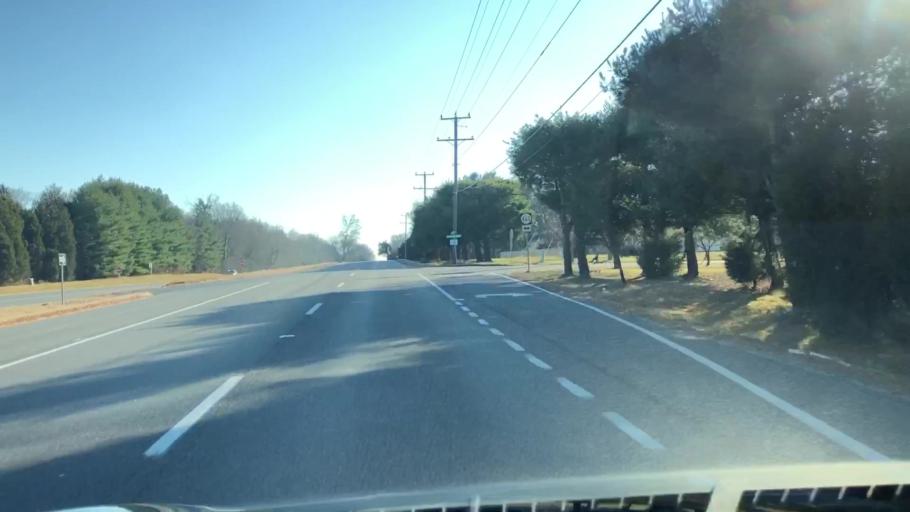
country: US
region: Virginia
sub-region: Fauquier County
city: Bealeton
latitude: 38.6003
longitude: -77.8008
